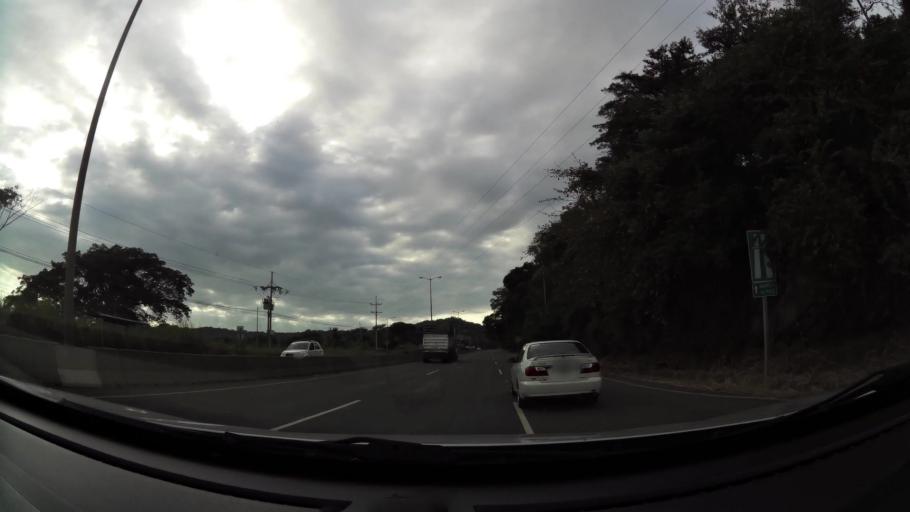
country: CR
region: Puntarenas
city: Esparza
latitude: 9.9139
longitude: -84.6765
